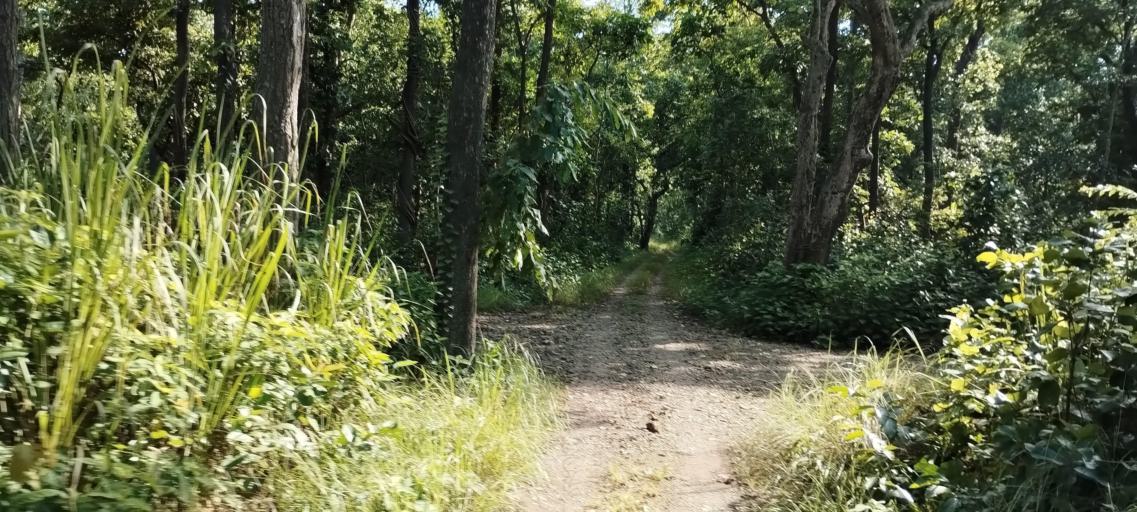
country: NP
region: Far Western
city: Tikapur
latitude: 28.5290
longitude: 81.2827
